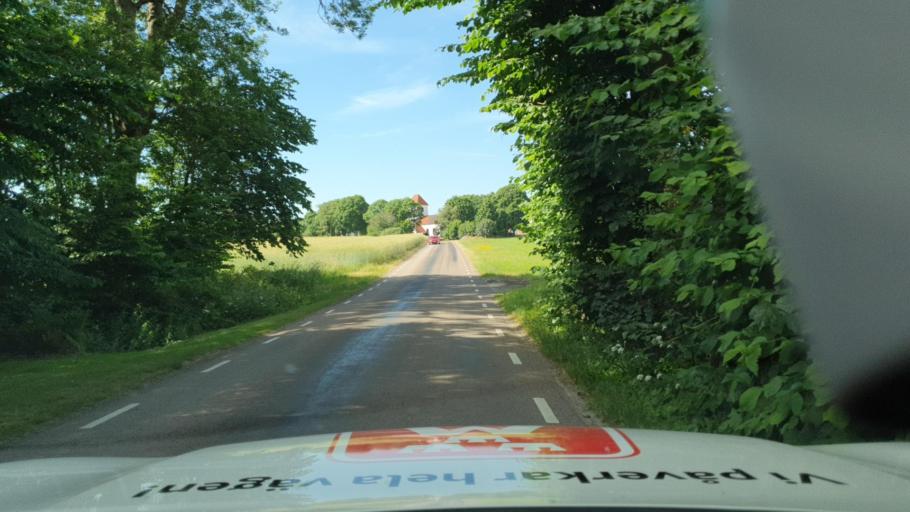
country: SE
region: Skane
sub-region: Sjobo Kommun
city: Blentarp
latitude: 55.6060
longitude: 13.5925
